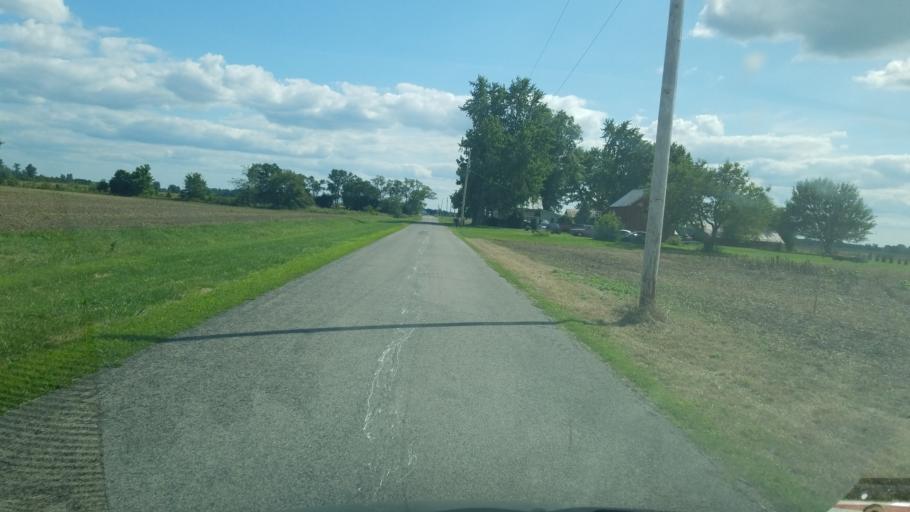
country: US
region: Ohio
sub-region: Logan County
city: Lakeview
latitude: 40.5268
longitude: -83.9749
